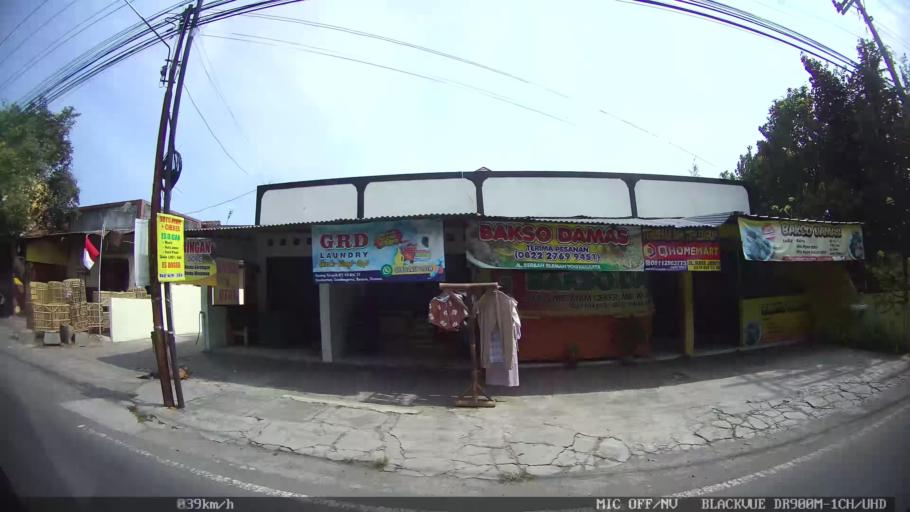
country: ID
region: Daerah Istimewa Yogyakarta
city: Depok
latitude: -7.8048
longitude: 110.4256
